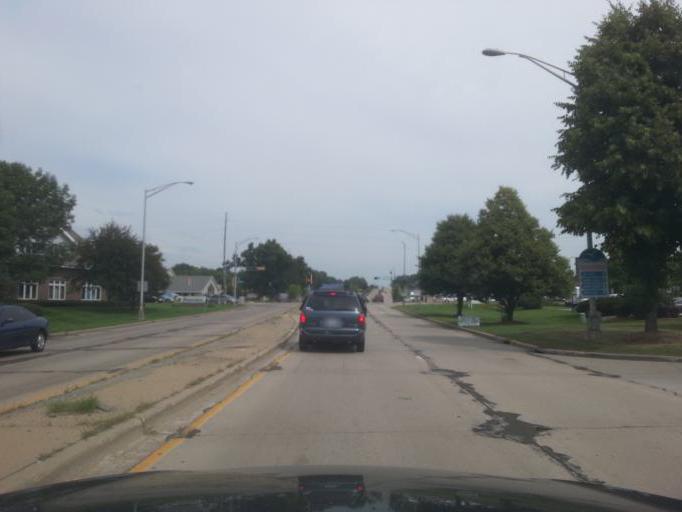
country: US
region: Wisconsin
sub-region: Dane County
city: Monona
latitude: 43.0468
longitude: -89.3245
